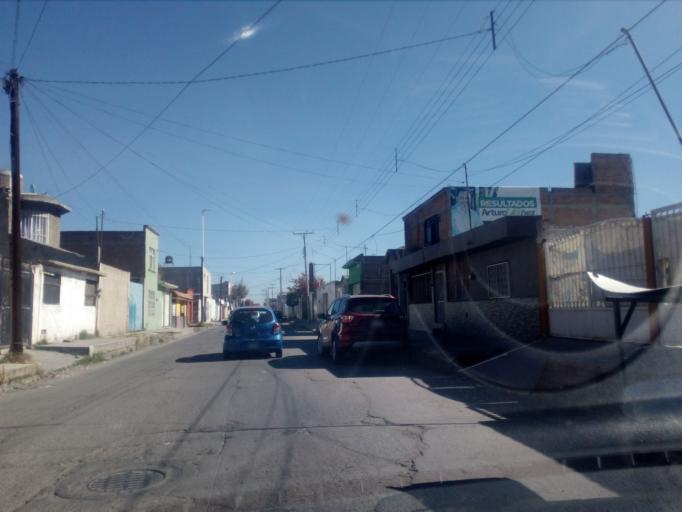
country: MX
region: Durango
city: Victoria de Durango
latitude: 24.0044
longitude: -104.6592
